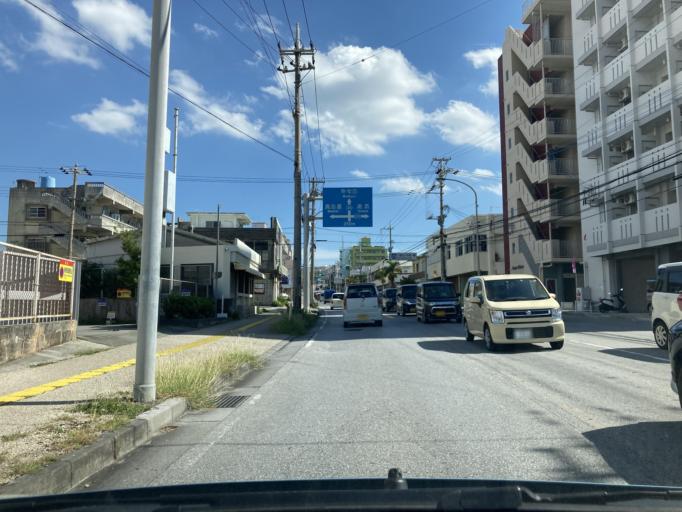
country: JP
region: Okinawa
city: Ginowan
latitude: 26.2685
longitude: 127.7336
